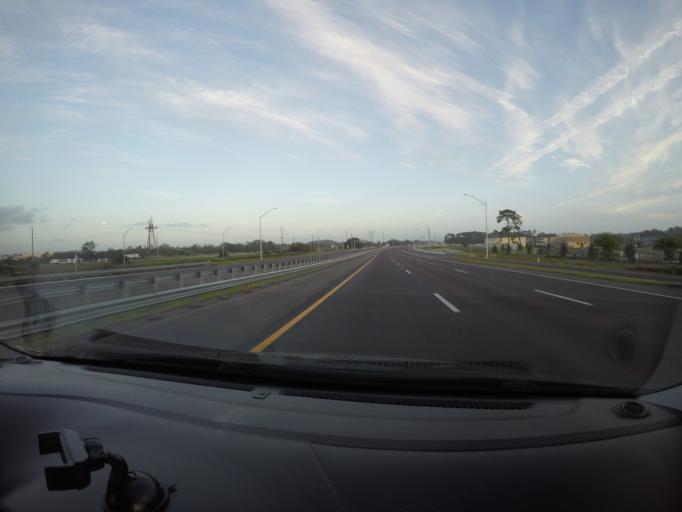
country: US
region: Florida
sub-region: Orange County
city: Azalea Park
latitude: 28.5127
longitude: -81.2489
